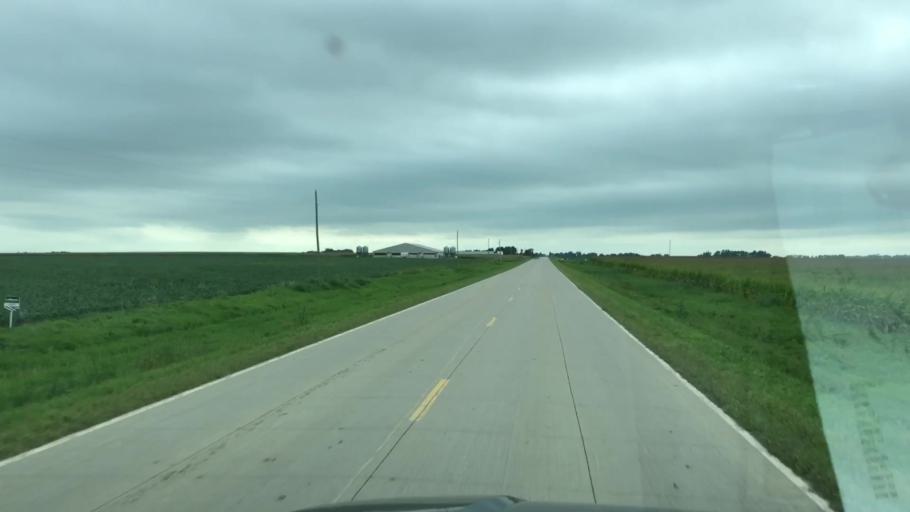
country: US
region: Iowa
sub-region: O'Brien County
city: Sheldon
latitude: 43.1309
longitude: -95.9791
